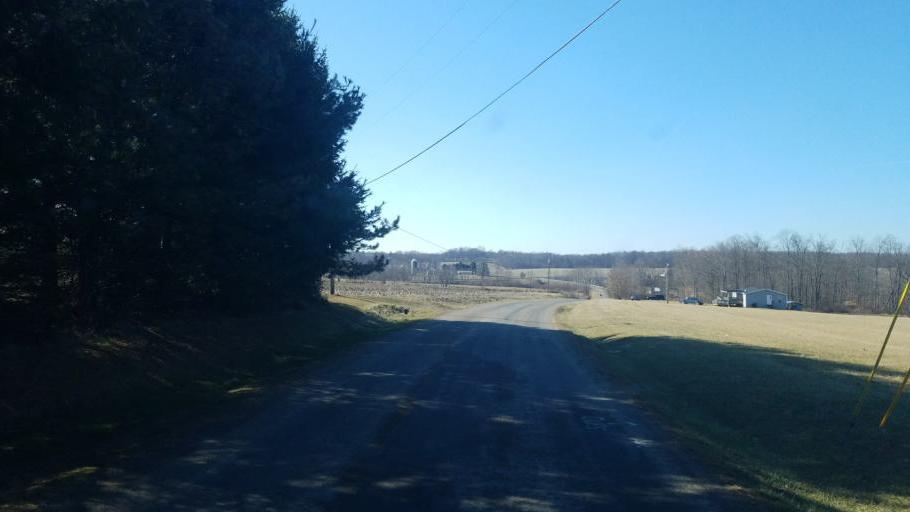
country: US
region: Ohio
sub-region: Sandusky County
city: Bellville
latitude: 40.5763
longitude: -82.5985
